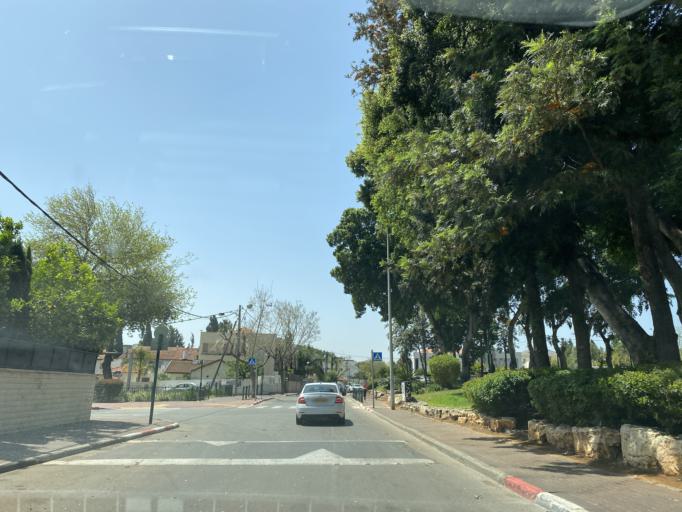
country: IL
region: Central District
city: Ra'anana
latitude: 32.1880
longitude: 34.8702
